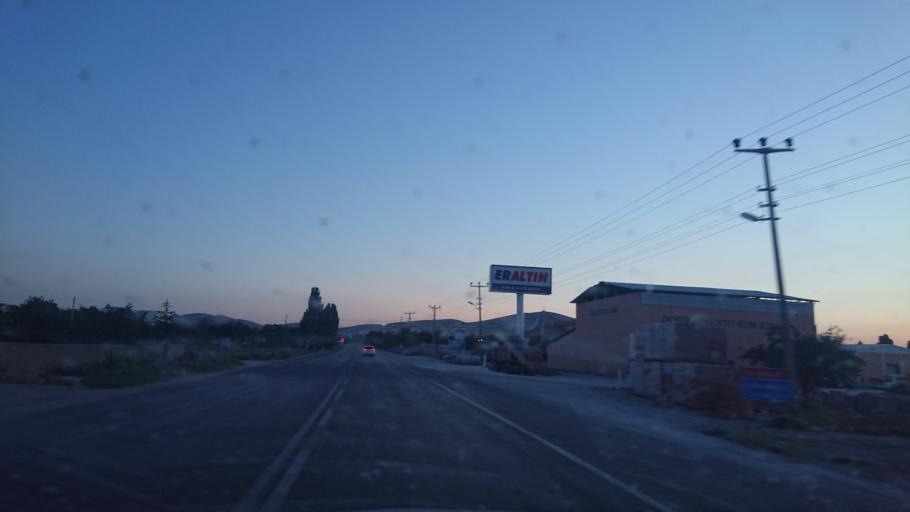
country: TR
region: Aksaray
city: Ortakoy
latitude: 38.7498
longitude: 34.0594
